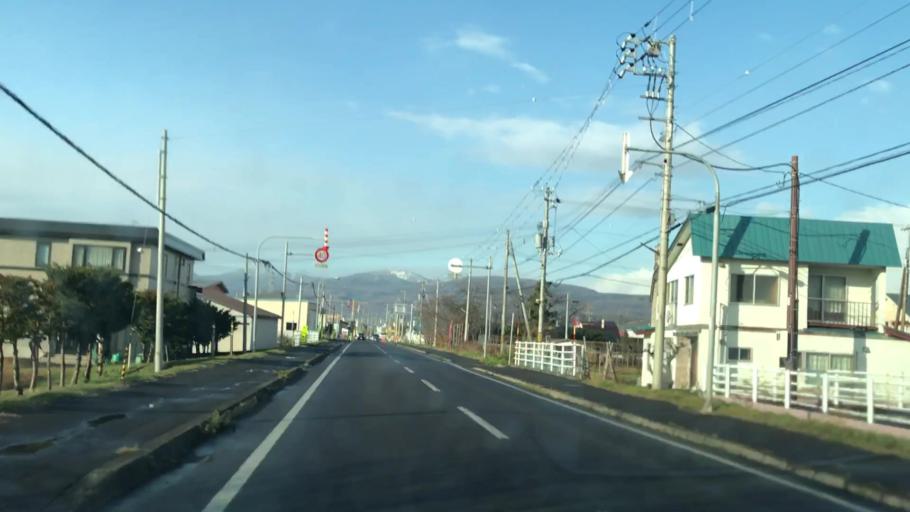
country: JP
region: Hokkaido
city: Yoichi
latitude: 43.1828
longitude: 140.8081
